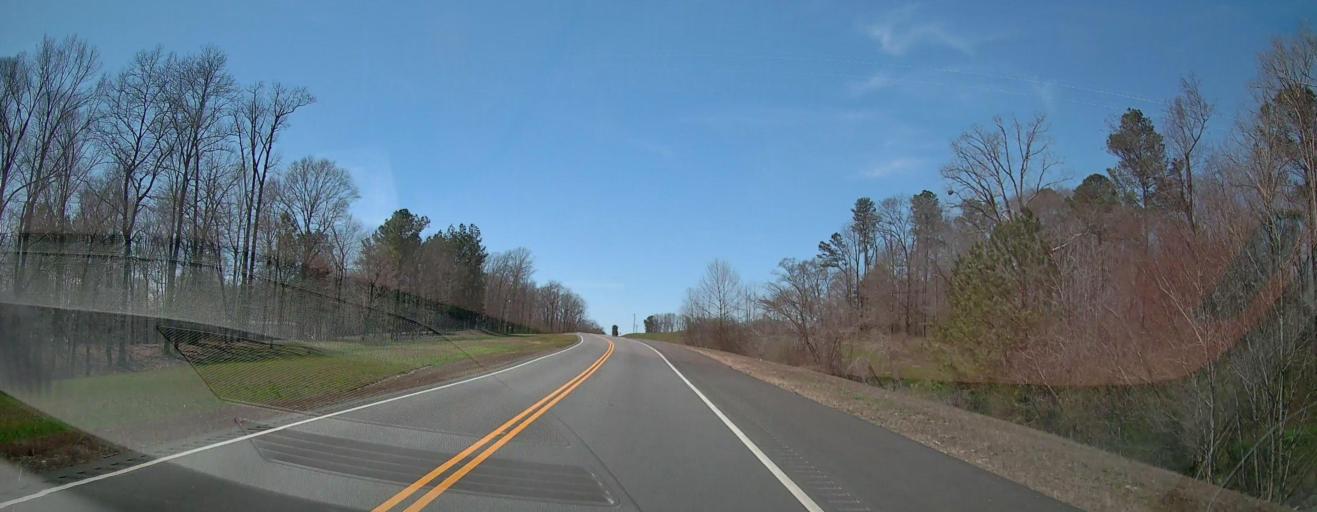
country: US
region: Alabama
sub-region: Blount County
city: Blountsville
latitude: 34.1739
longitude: -86.5633
